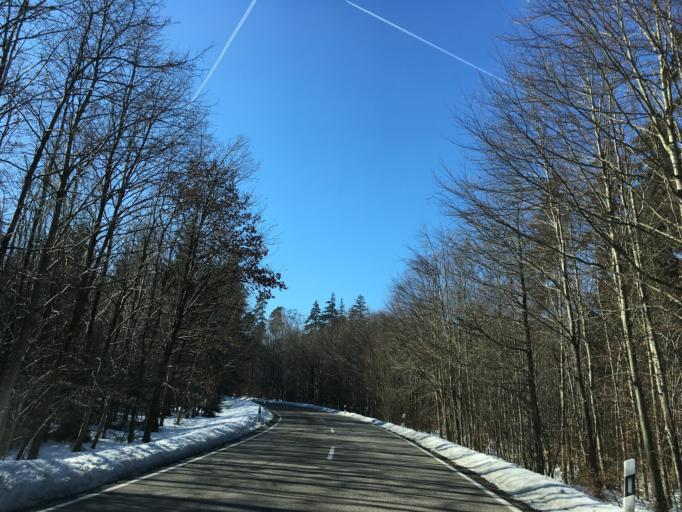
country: DE
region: Bavaria
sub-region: Upper Bavaria
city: Maitenbeth
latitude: 48.1280
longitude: 12.0789
